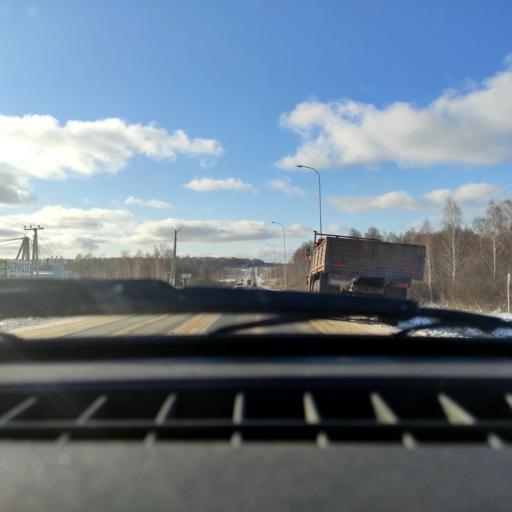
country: RU
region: Bashkortostan
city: Iglino
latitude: 54.8173
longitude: 56.3710
